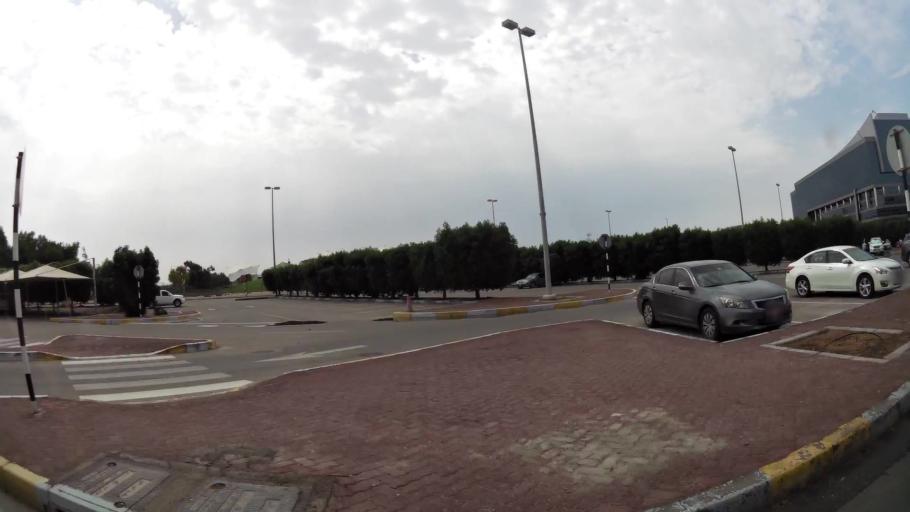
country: AE
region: Abu Dhabi
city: Abu Dhabi
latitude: 24.4296
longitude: 54.4673
